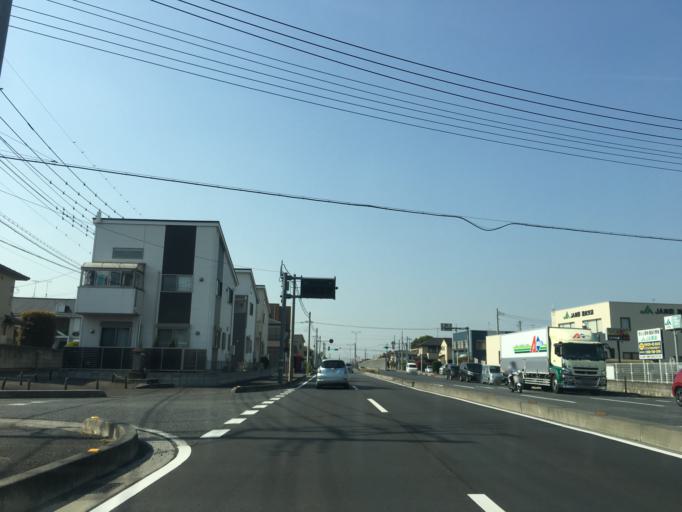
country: JP
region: Saitama
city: Hasuda
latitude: 35.9831
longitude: 139.6579
